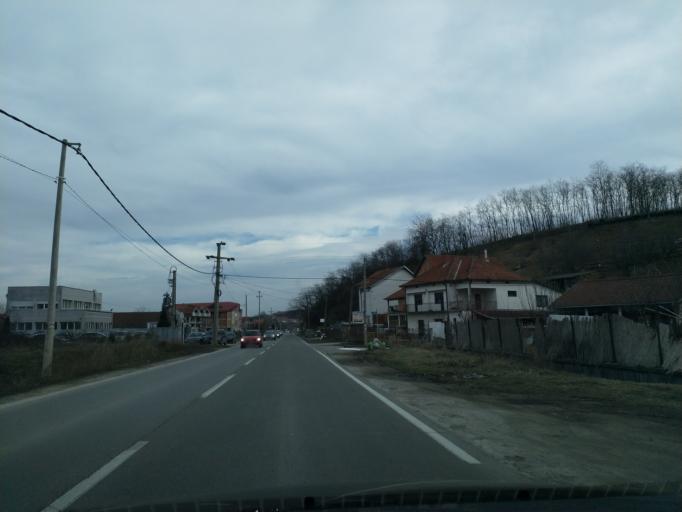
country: RS
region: Central Serbia
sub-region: Belgrade
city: Zvezdara
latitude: 44.7280
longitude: 20.5658
